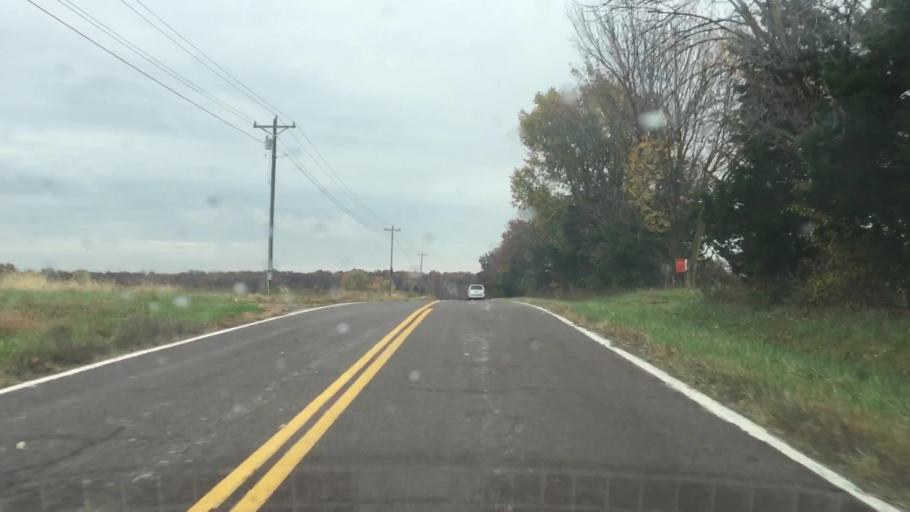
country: US
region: Missouri
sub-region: Callaway County
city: Fulton
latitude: 38.7879
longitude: -91.7834
